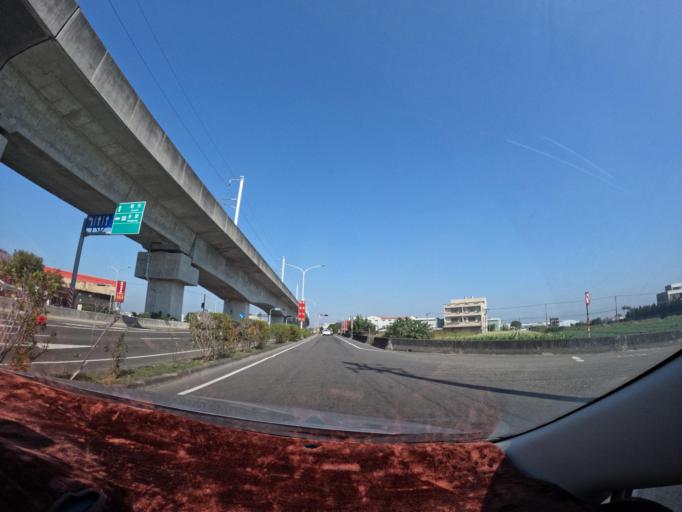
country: TW
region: Taiwan
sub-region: Tainan
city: Tainan
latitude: 23.0228
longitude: 120.2892
